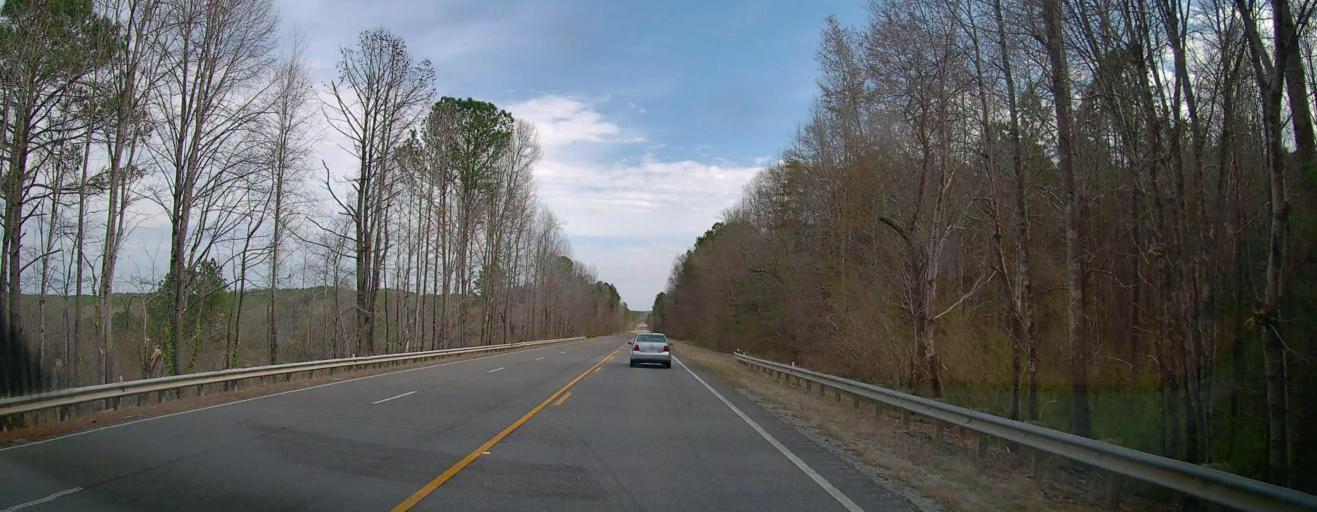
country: US
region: Alabama
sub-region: Walker County
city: Carbon Hill
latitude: 33.9149
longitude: -87.5649
